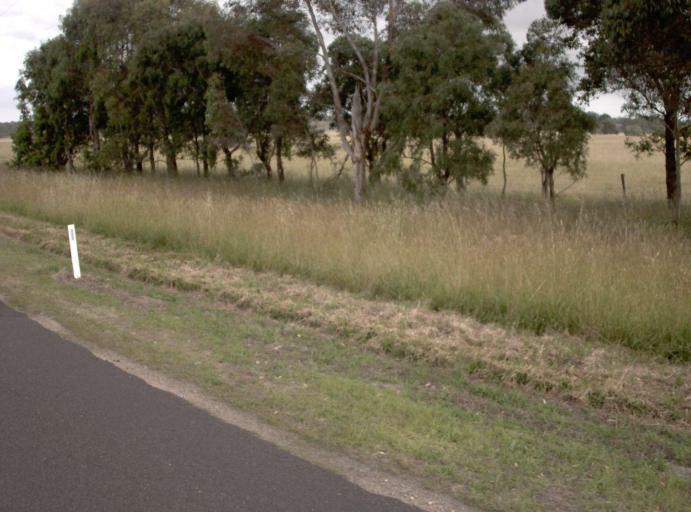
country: AU
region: Victoria
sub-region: Wellington
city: Sale
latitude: -37.8522
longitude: 147.0481
